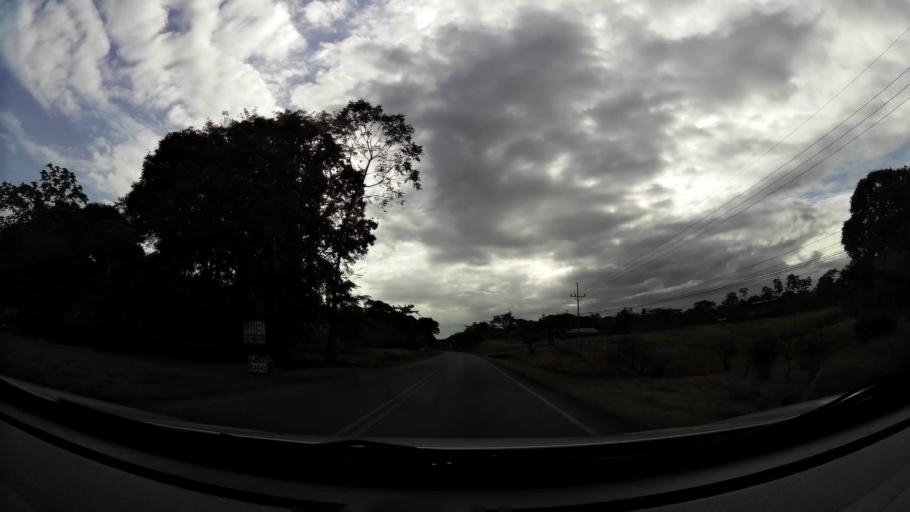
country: CR
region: Limon
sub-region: Canton de Guacimo
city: Guacimo
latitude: 10.2023
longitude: -83.6778
